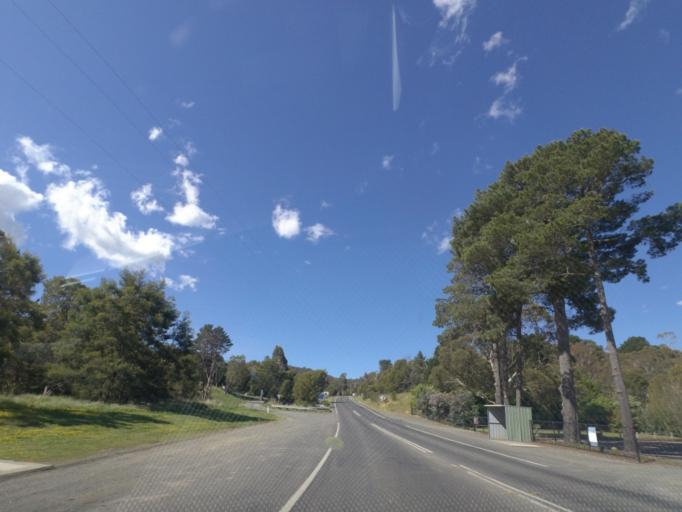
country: AU
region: Victoria
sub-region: Moorabool
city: Bacchus Marsh
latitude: -37.5605
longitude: 144.2991
